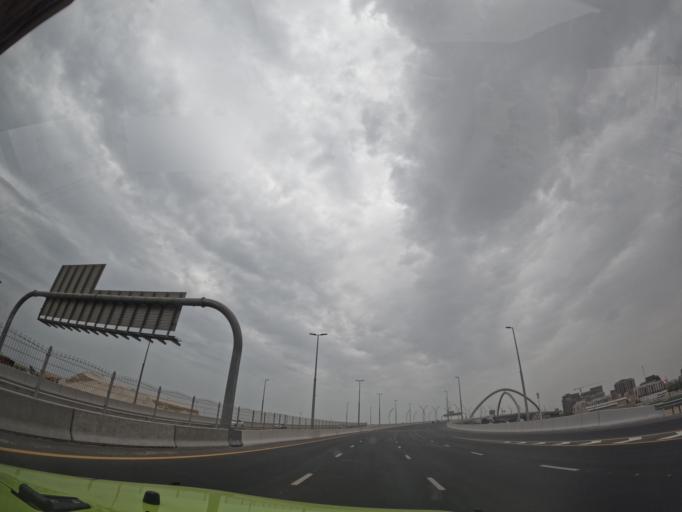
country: AE
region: Ash Shariqah
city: Sharjah
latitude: 25.2718
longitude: 55.2905
